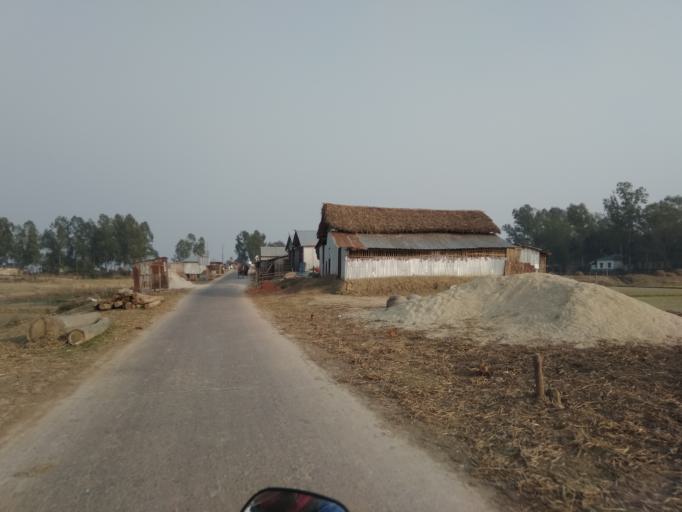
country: BD
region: Rajshahi
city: Ishurdi
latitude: 24.4934
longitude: 89.1990
